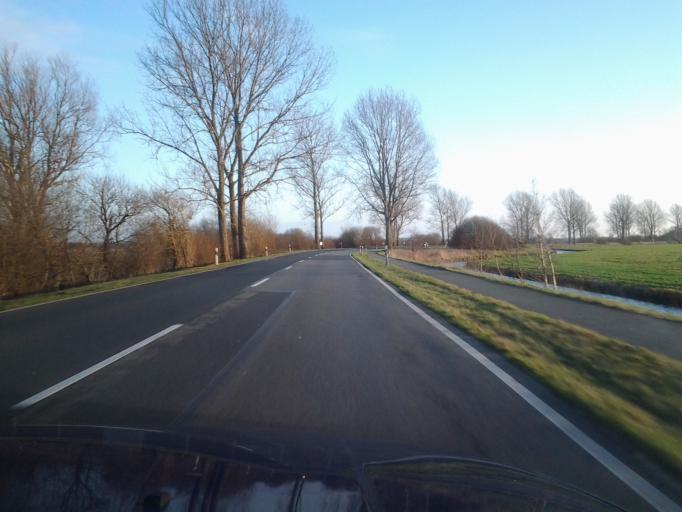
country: DE
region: Lower Saxony
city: Osterholz-Scharmbeck
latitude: 53.2118
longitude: 8.8172
